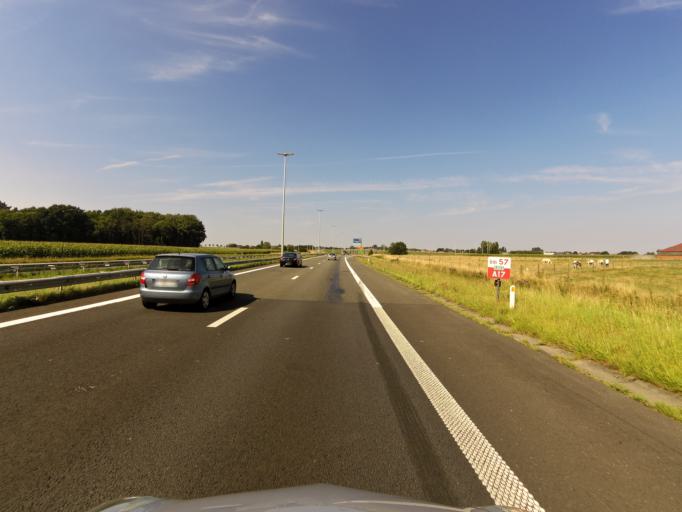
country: BE
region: Flanders
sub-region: Provincie West-Vlaanderen
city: Lichtervelde
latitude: 51.0736
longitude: 3.1533
